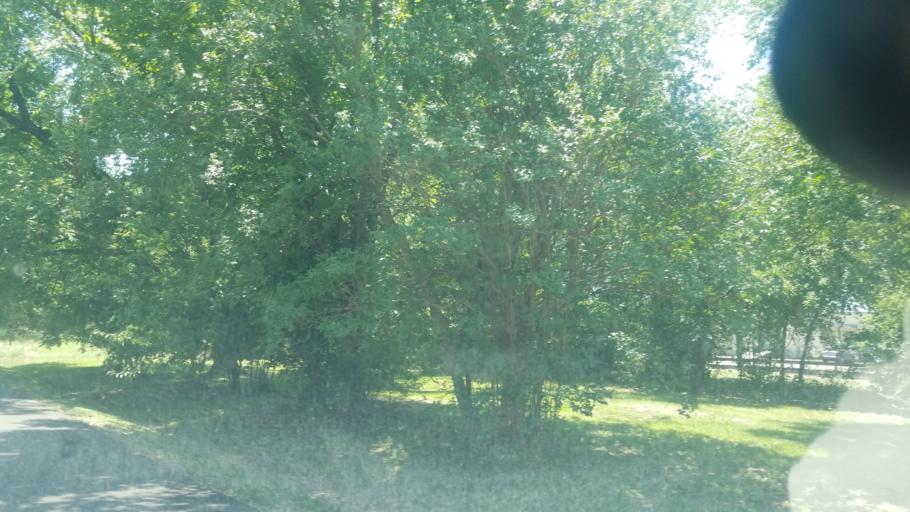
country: US
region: Texas
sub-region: Dallas County
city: Dallas
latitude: 32.7384
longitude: -96.7848
